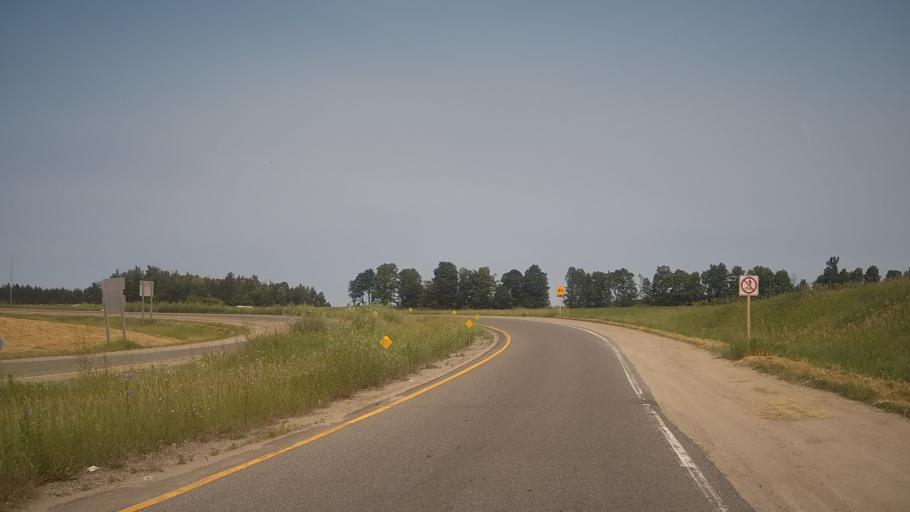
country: CA
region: Ontario
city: Barrie
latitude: 44.4778
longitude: -79.6942
